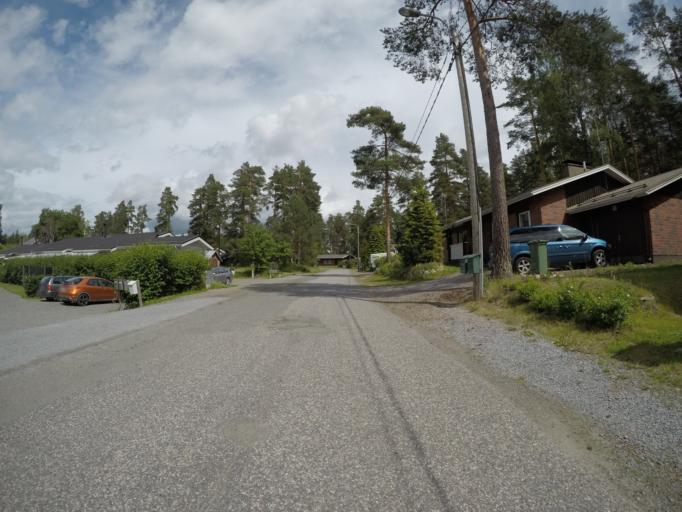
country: FI
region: Haeme
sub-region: Haemeenlinna
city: Haemeenlinna
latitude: 60.9707
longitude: 24.4340
